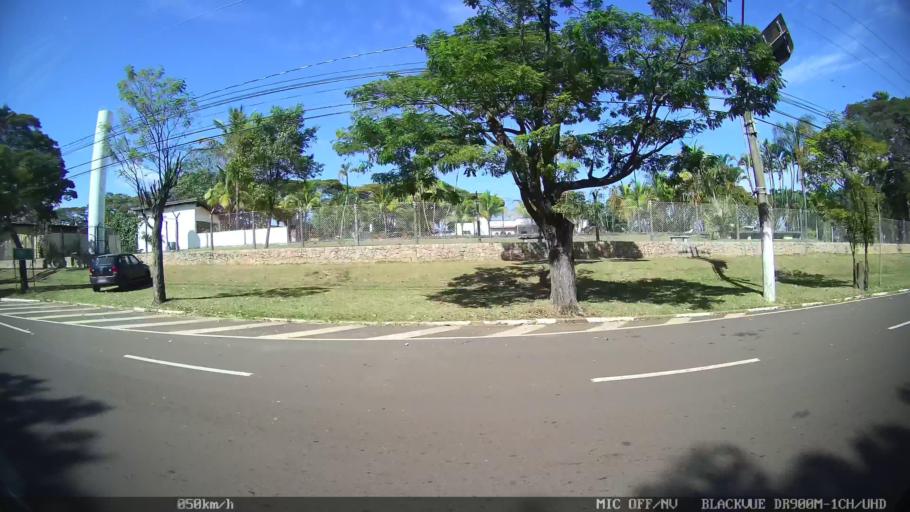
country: BR
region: Sao Paulo
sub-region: Franca
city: Franca
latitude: -20.5410
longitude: -47.4186
